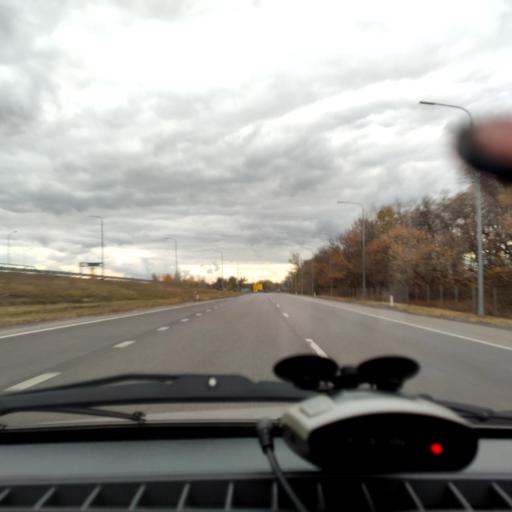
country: RU
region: Voronezj
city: Podgornoye
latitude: 51.8364
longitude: 39.2137
